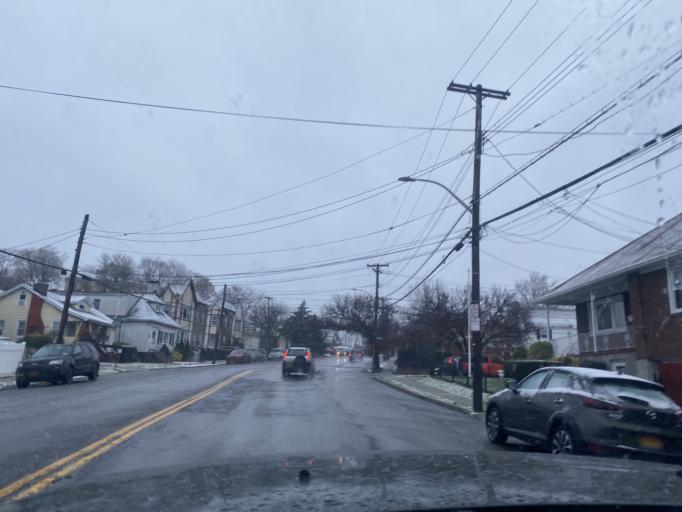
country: US
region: New York
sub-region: Westchester County
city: Mount Vernon
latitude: 40.9050
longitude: -73.8674
